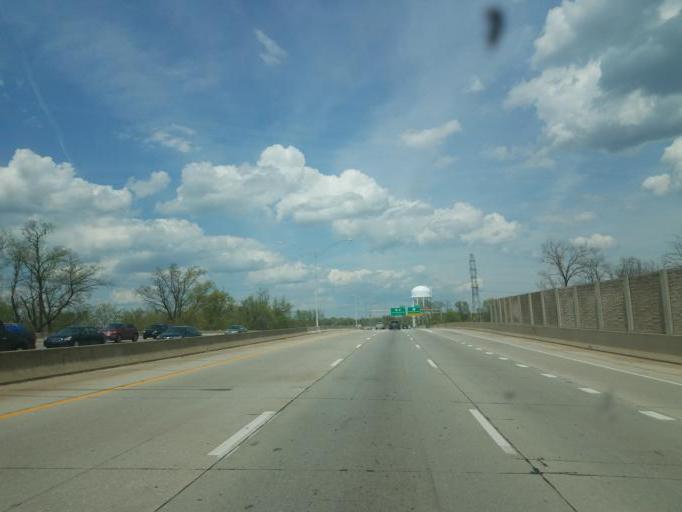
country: US
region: Kentucky
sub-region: Jefferson County
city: Beechwood Village
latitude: 38.2590
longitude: -85.6229
